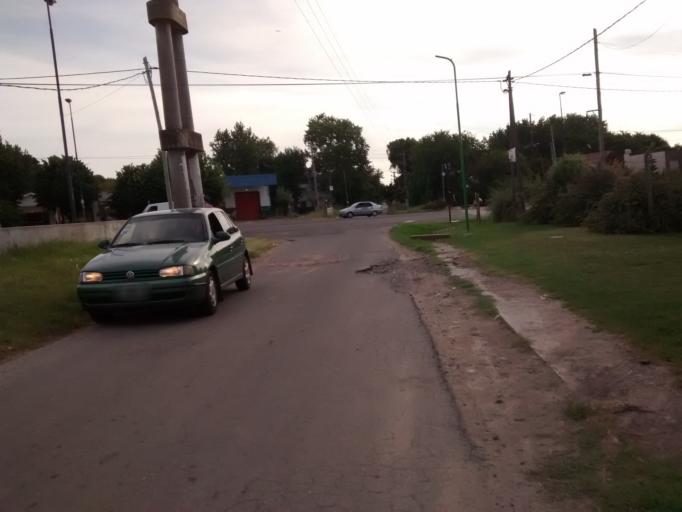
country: AR
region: Buenos Aires
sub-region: Partido de La Plata
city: La Plata
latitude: -34.8489
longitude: -58.0938
